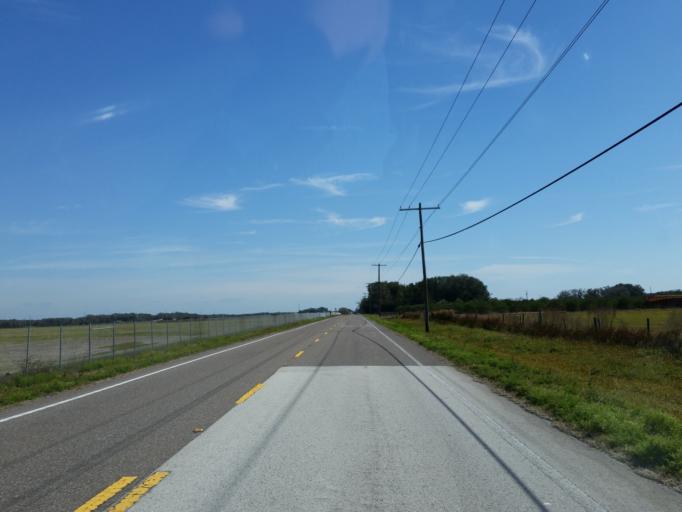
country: US
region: Florida
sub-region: Hillsborough County
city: Boyette
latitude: 27.7626
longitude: -82.1967
